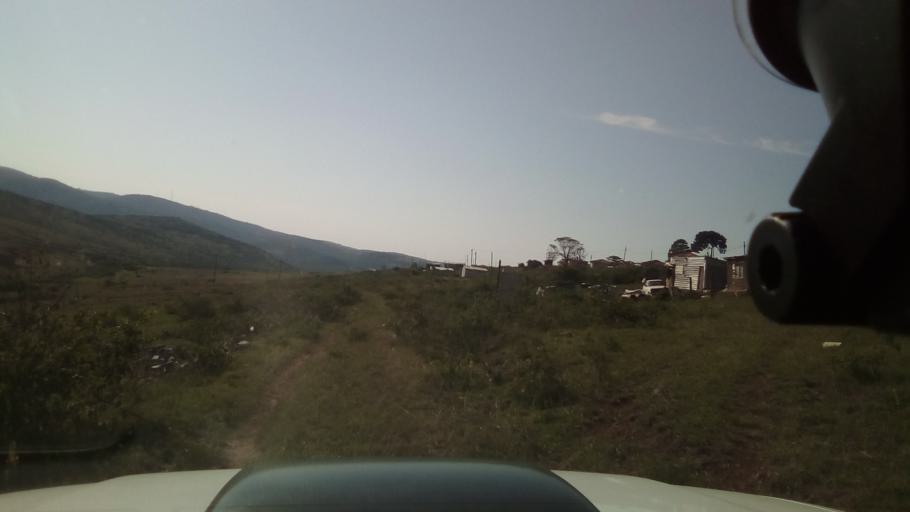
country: ZA
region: Eastern Cape
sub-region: Buffalo City Metropolitan Municipality
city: East London
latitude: -32.8397
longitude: 27.9915
